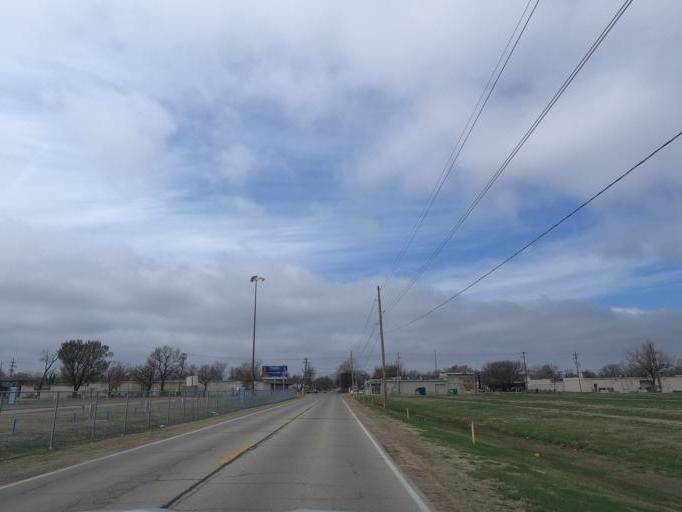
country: US
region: Kansas
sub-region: Reno County
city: Hutchinson
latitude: 38.0811
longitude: -97.9298
